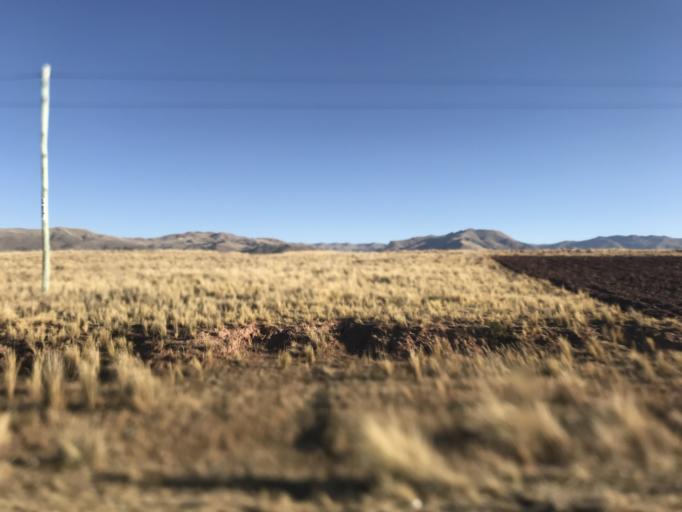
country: BO
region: La Paz
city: Tiahuanaco
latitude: -16.5634
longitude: -68.6236
